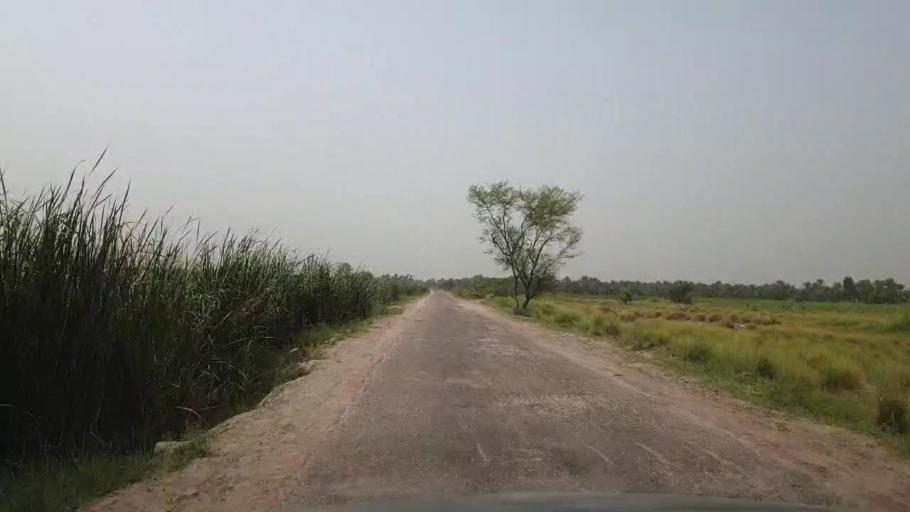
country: PK
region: Sindh
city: Gambat
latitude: 27.3859
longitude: 68.5486
